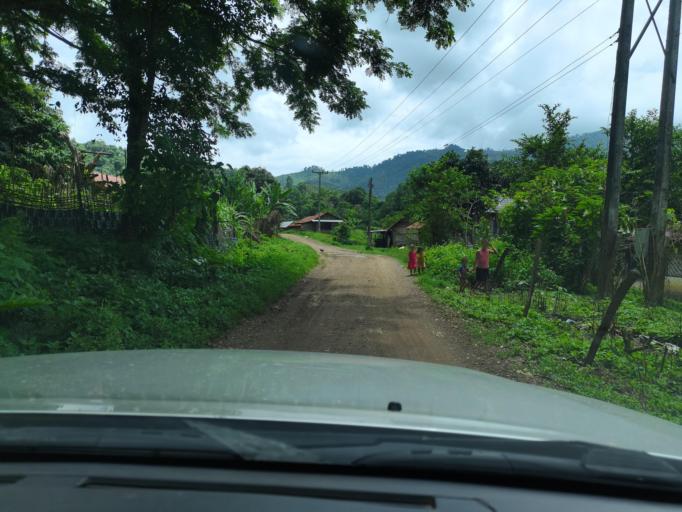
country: LA
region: Loungnamtha
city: Muang Long
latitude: 20.7445
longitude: 101.0184
